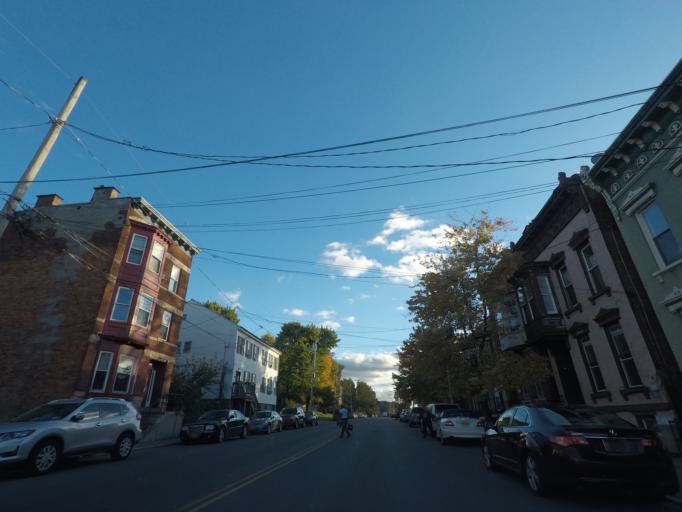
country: US
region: New York
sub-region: Albany County
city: Green Island
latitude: 42.7390
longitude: -73.6819
